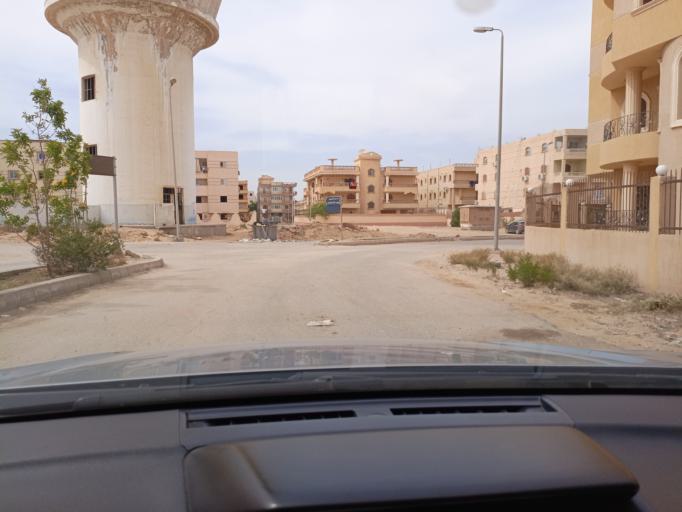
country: EG
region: Muhafazat al Qalyubiyah
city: Al Khankah
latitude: 30.2423
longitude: 31.4845
